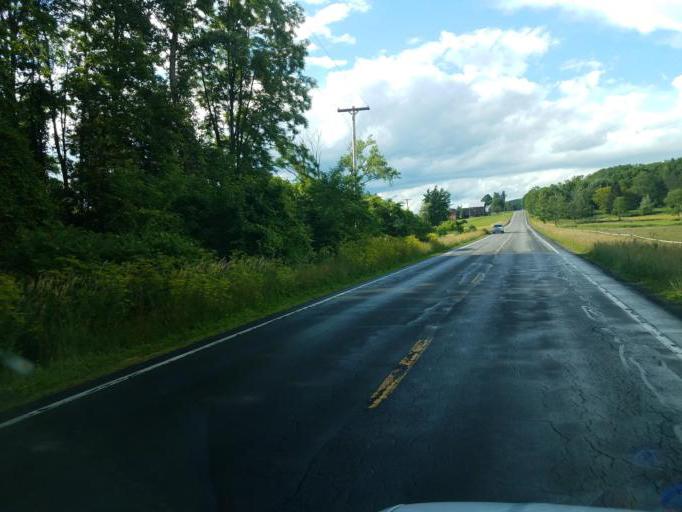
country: US
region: New York
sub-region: Wayne County
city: Clyde
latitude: 43.0291
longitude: -76.8621
